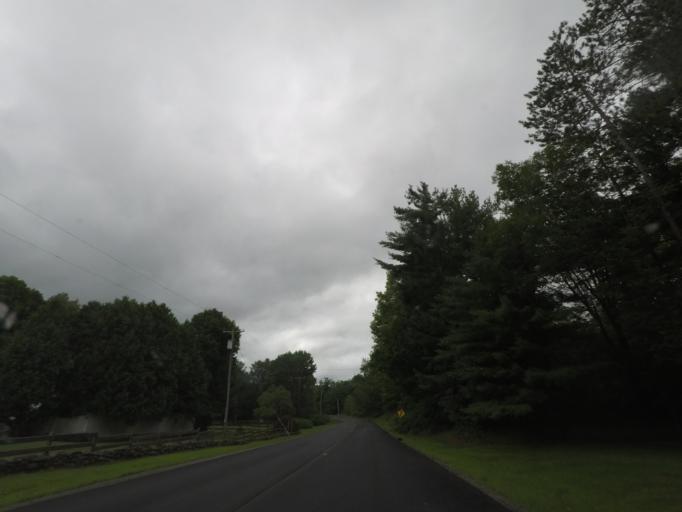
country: US
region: New York
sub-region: Rensselaer County
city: Poestenkill
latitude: 42.6892
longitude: -73.4867
